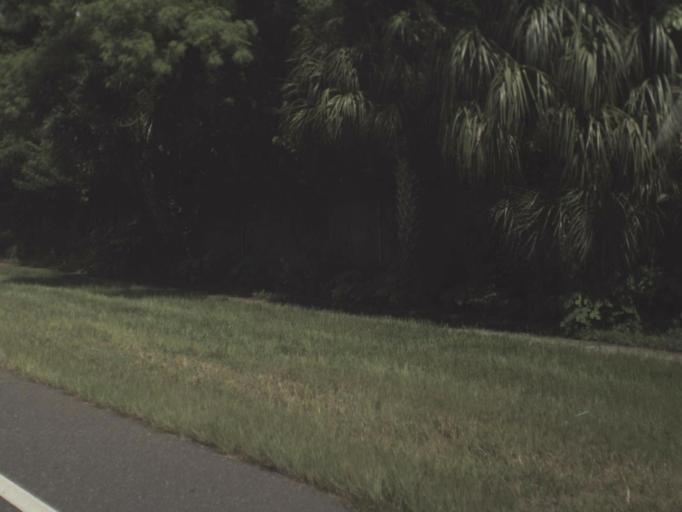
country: US
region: Florida
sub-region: Hillsborough County
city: East Lake-Orient Park
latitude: 27.9723
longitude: -82.4099
